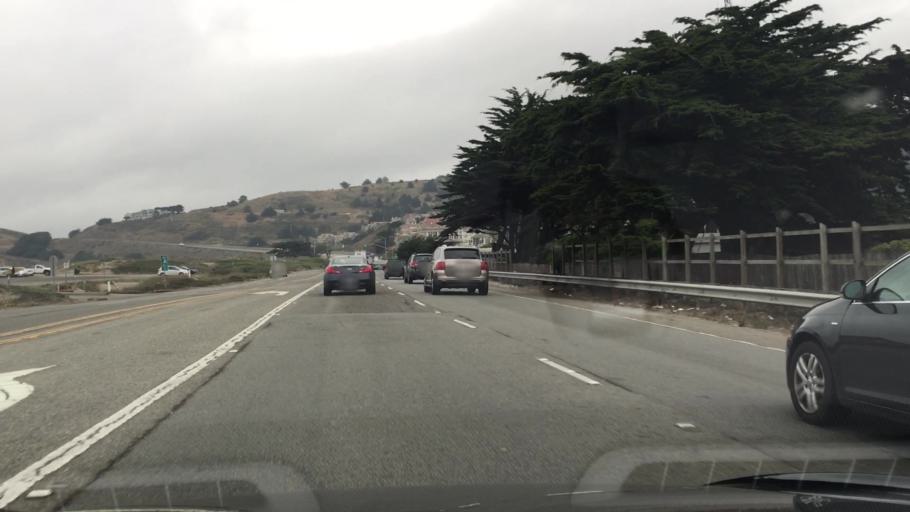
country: US
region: California
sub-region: San Mateo County
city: Pacifica
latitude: 37.5962
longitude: -122.5047
